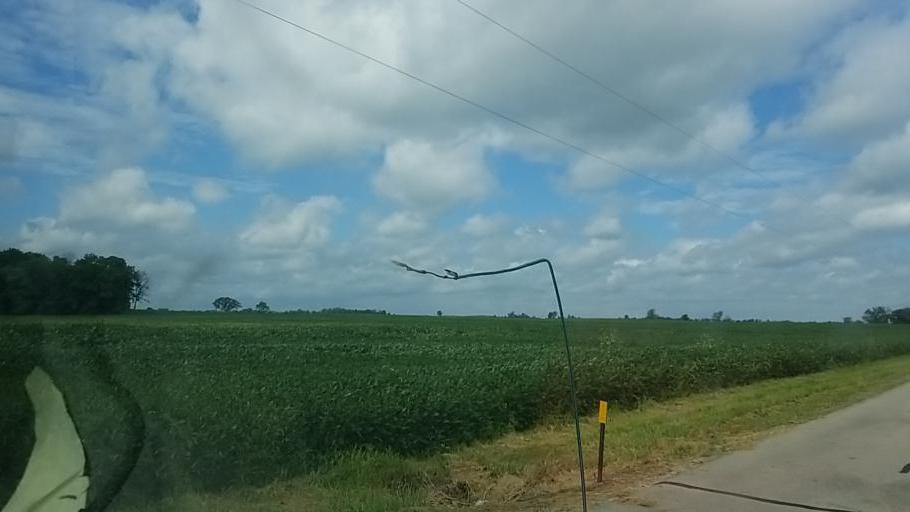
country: US
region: Ohio
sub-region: Fayette County
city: Jeffersonville
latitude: 39.6878
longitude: -83.5765
